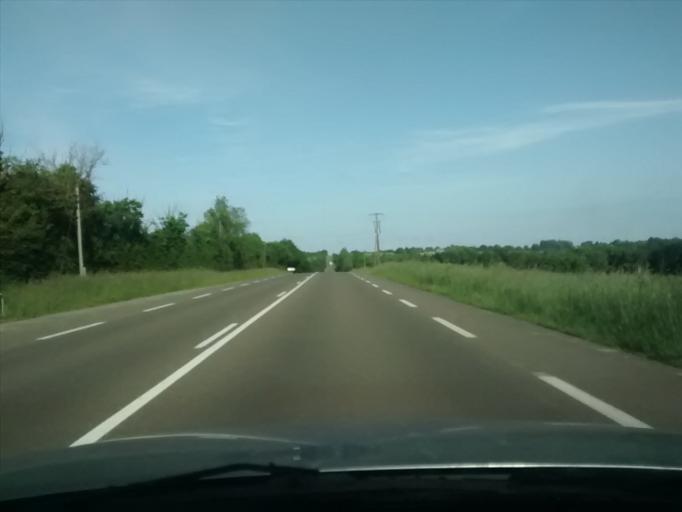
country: FR
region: Pays de la Loire
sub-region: Departement de la Mayenne
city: Soulge-sur-Ouette
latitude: 48.0537
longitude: -0.5444
